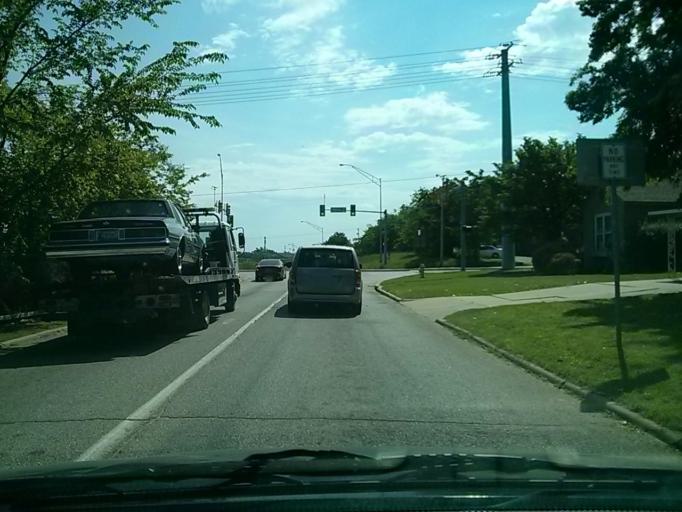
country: US
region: Oklahoma
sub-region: Tulsa County
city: Tulsa
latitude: 36.1590
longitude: -95.9410
